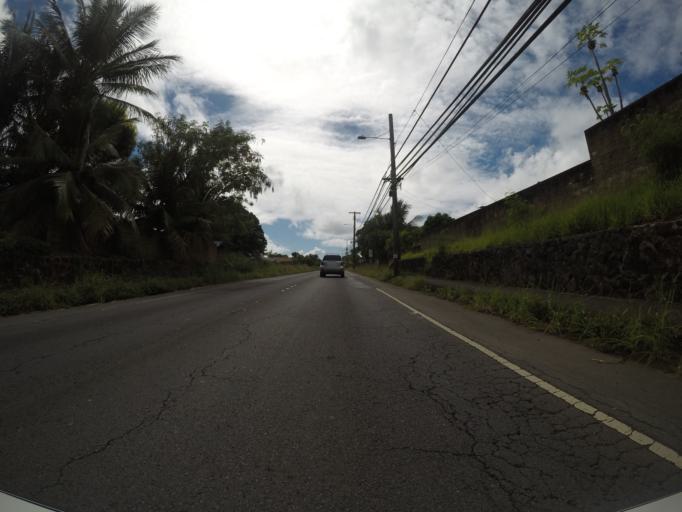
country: US
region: Hawaii
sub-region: Honolulu County
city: Waimanalo
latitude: 21.3476
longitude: -157.7198
